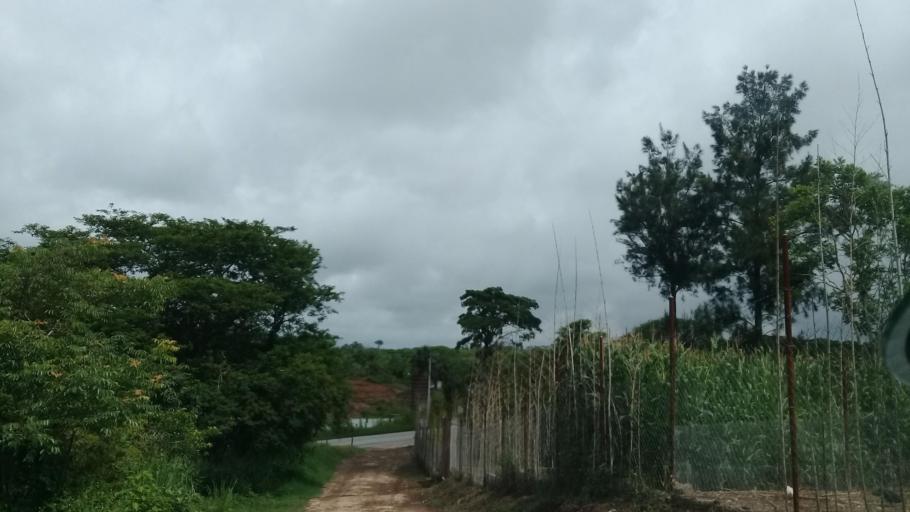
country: MX
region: Veracruz
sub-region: Emiliano Zapata
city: Jacarandas
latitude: 19.4844
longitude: -96.8567
